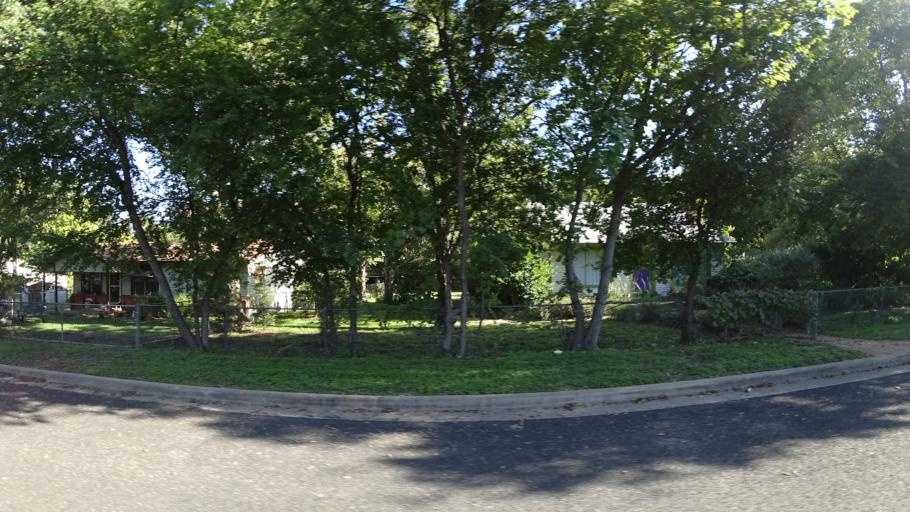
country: US
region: Texas
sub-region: Travis County
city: Austin
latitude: 30.3505
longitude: -97.6993
